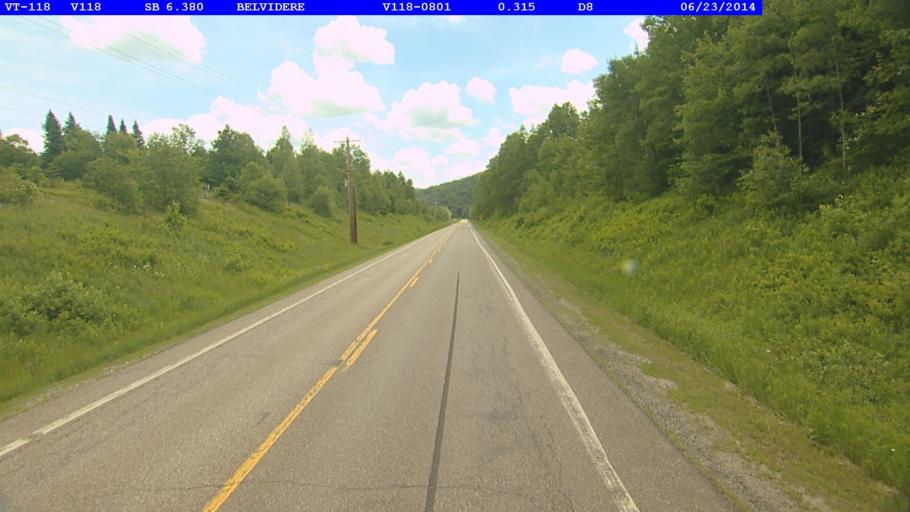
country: US
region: Vermont
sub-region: Lamoille County
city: Johnson
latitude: 44.7657
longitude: -72.6211
